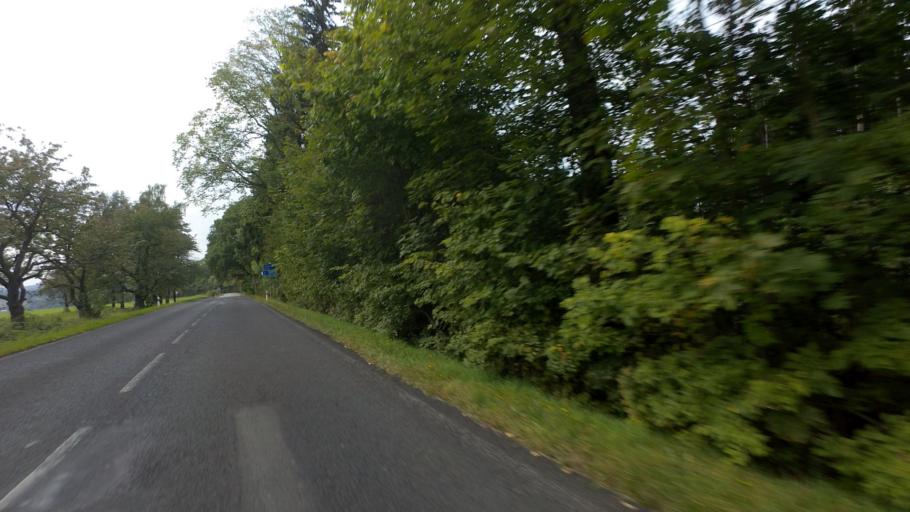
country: CZ
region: Ustecky
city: Velky Senov
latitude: 51.0069
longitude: 14.3778
